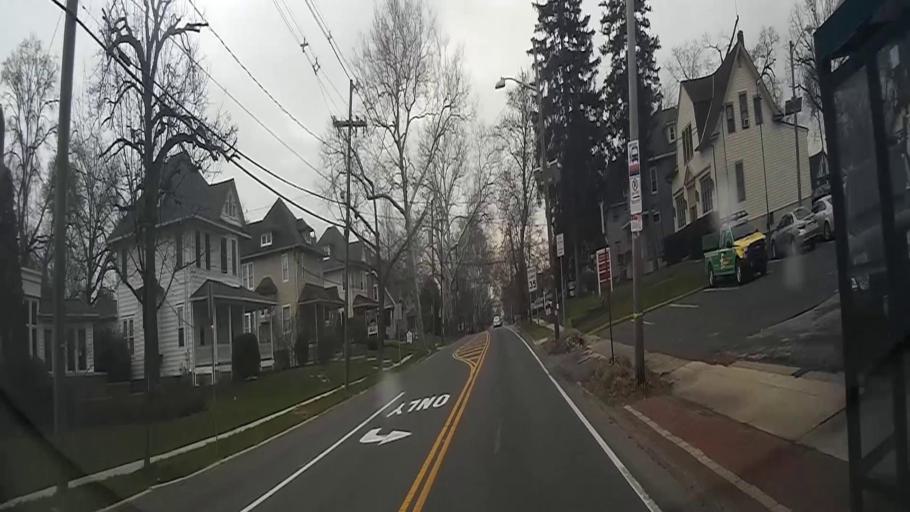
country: US
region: New Jersey
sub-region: Camden County
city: Haddon Heights
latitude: 39.8831
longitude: -75.0569
